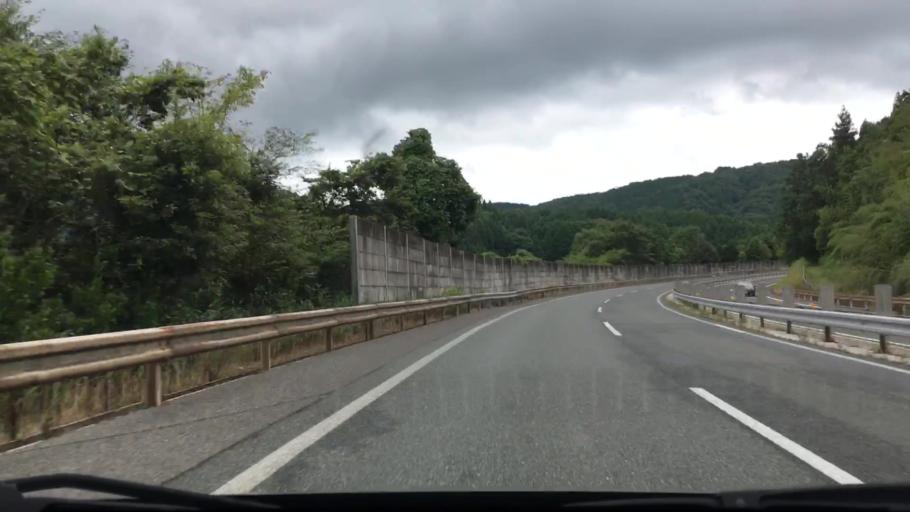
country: JP
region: Okayama
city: Niimi
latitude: 34.9051
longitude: 133.3020
